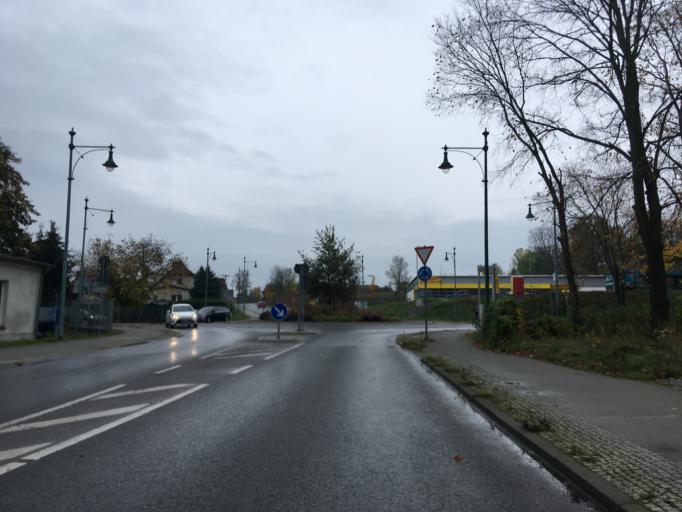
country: DE
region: Brandenburg
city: Beeskow
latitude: 52.1676
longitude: 14.2584
